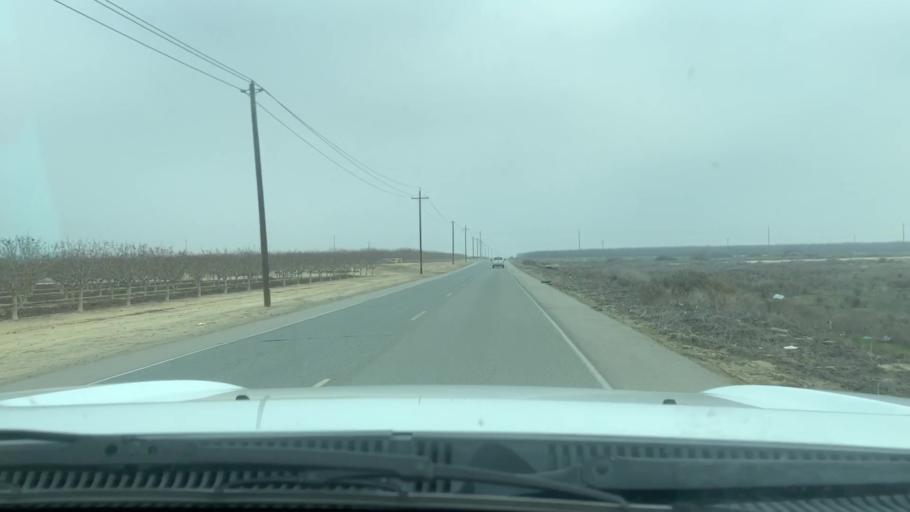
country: US
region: California
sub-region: Kern County
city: Buttonwillow
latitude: 35.5005
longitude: -119.4445
